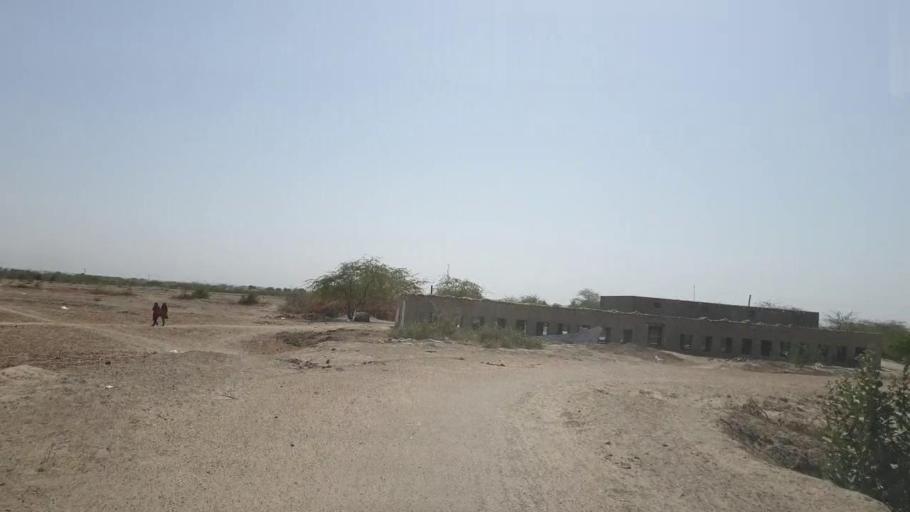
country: PK
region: Sindh
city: Naukot
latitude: 24.9607
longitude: 69.5190
